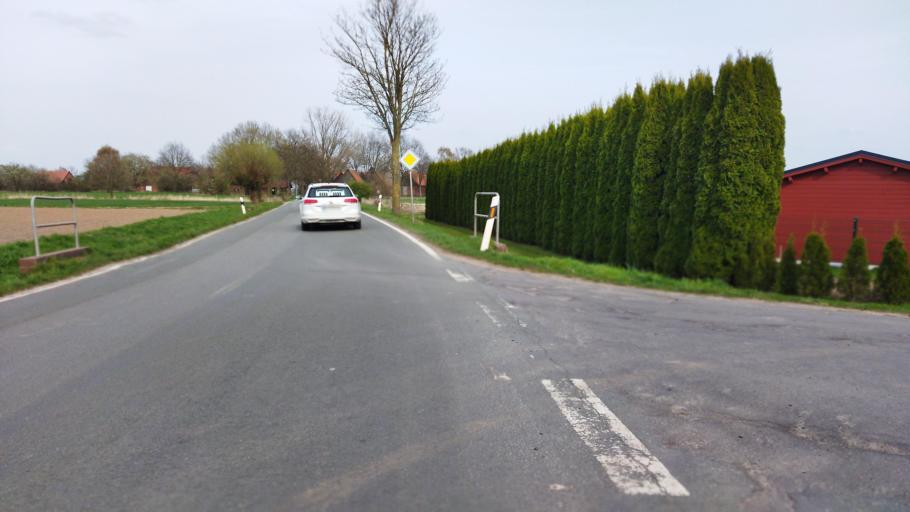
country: DE
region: Lower Saxony
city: Stolzenau
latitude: 52.4832
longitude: 9.0599
